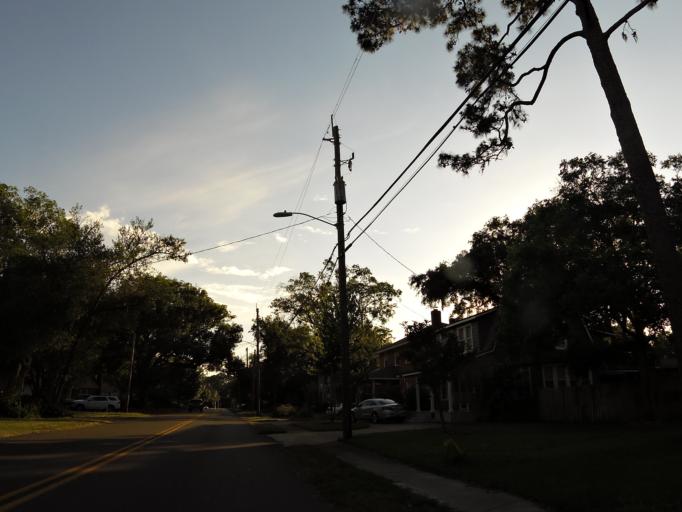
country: US
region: Florida
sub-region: Duval County
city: Jacksonville
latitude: 30.2977
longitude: -81.7153
